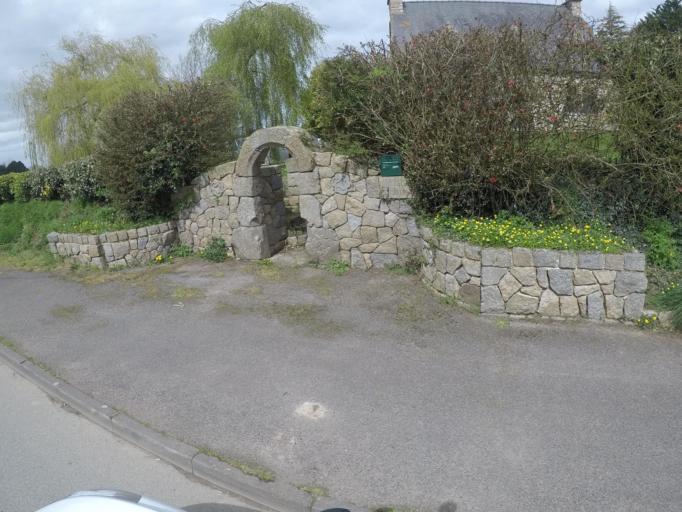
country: FR
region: Brittany
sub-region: Departement des Cotes-d'Armor
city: Plouha
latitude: 48.6794
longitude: -2.9251
